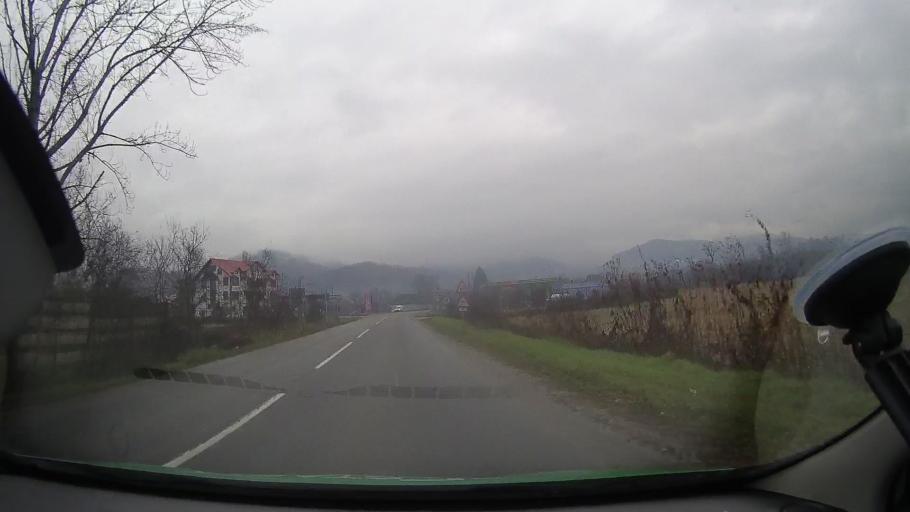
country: RO
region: Arad
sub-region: Comuna Gurahont
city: Gurahont
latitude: 46.2740
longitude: 22.3329
